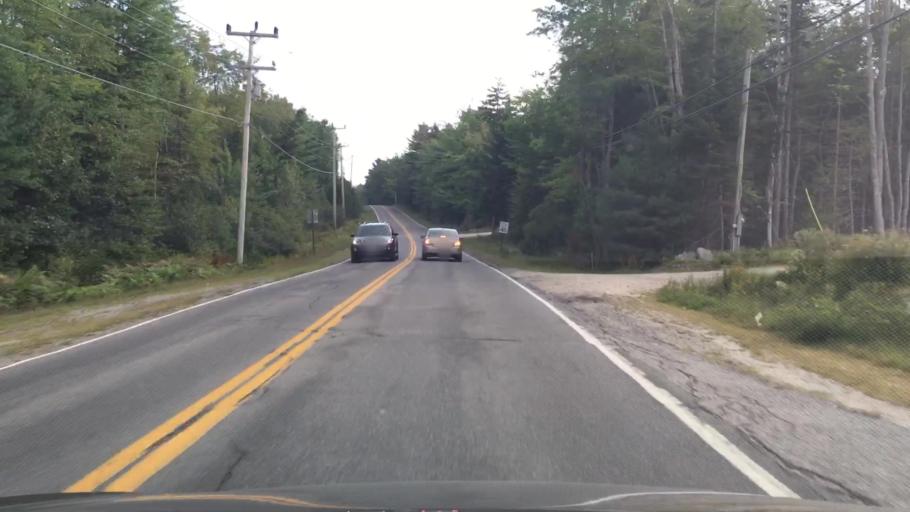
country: US
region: Maine
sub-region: Hancock County
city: Surry
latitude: 44.4404
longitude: -68.5695
